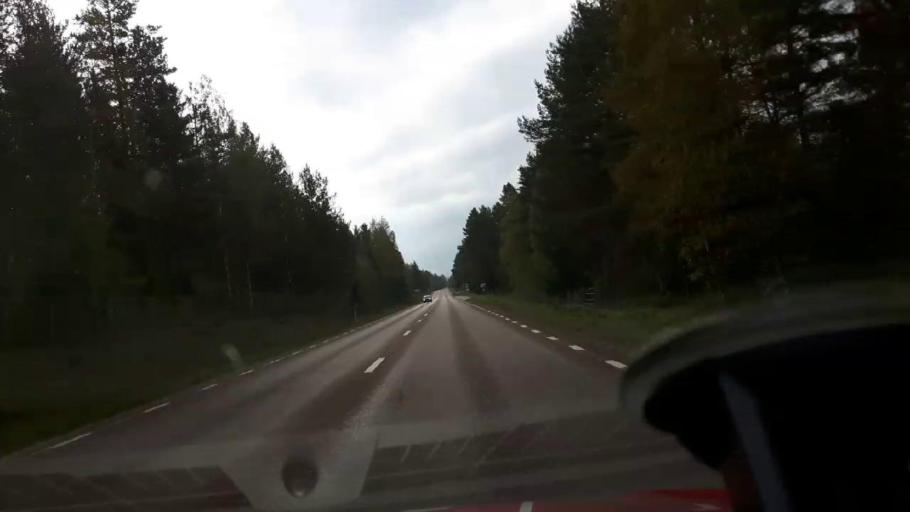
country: SE
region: Gaevleborg
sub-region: Bollnas Kommun
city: Kilafors
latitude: 61.2576
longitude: 16.5526
